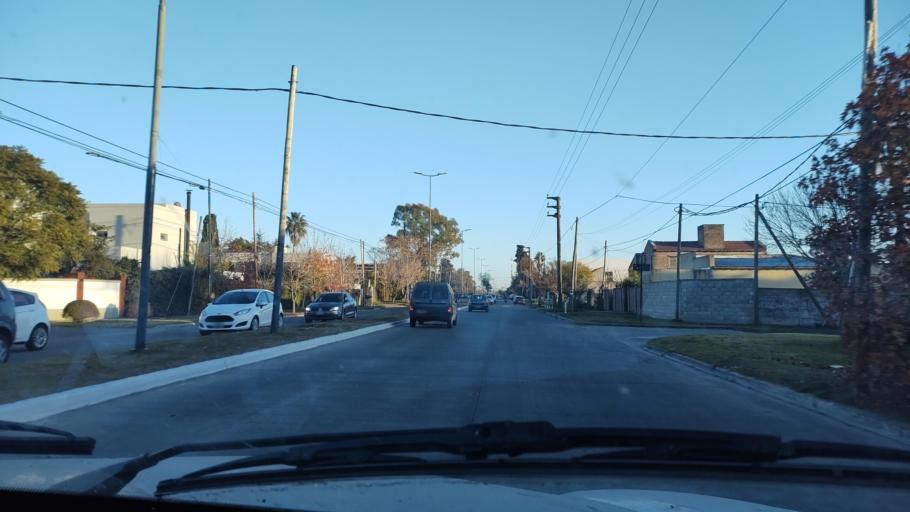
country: AR
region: Buenos Aires
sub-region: Partido de La Plata
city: La Plata
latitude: -34.8964
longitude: -58.0154
